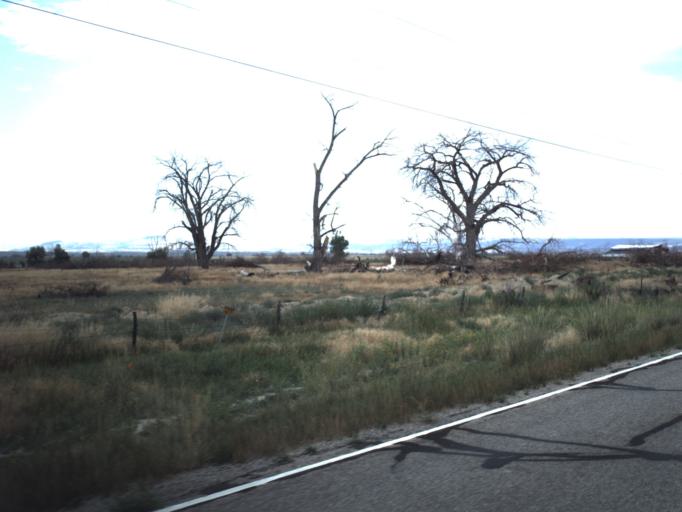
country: US
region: Utah
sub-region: Emery County
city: Huntington
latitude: 39.4162
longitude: -110.8565
